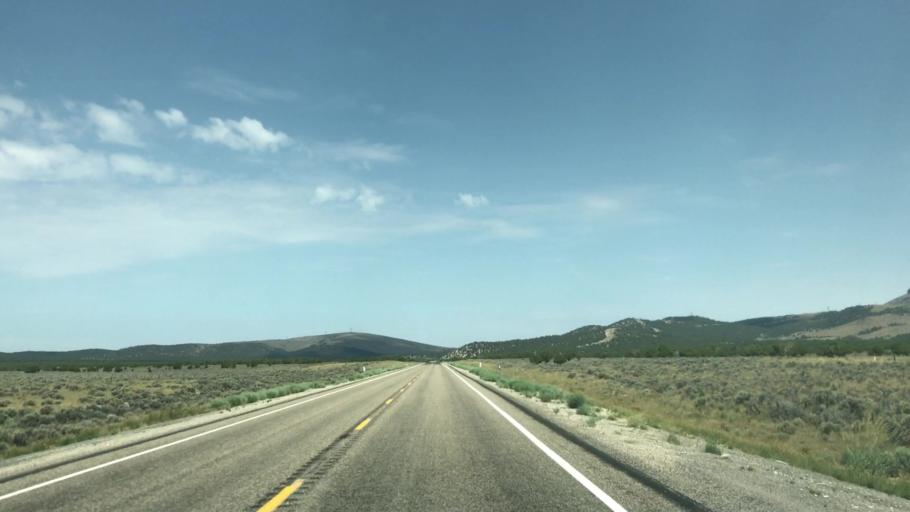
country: US
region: Nevada
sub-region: White Pine County
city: Ely
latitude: 39.3664
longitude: -115.0532
